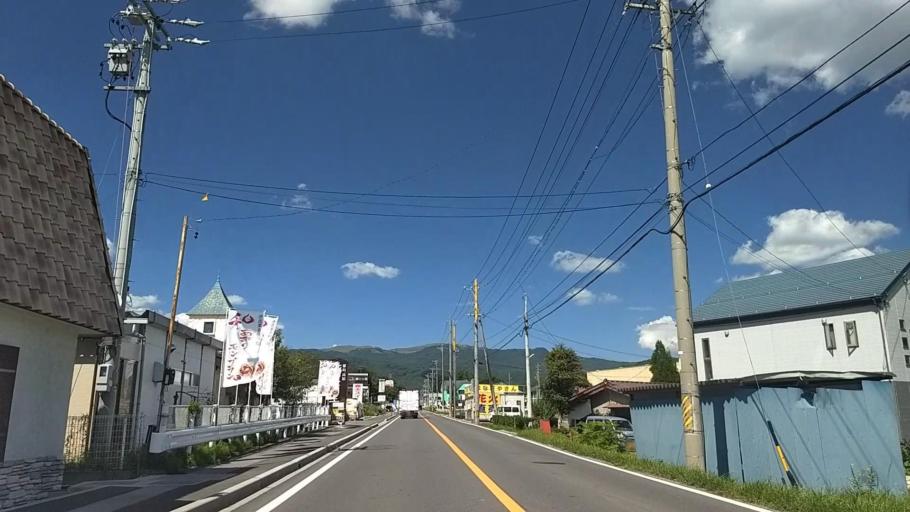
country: JP
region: Nagano
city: Chino
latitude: 36.0090
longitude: 138.1750
